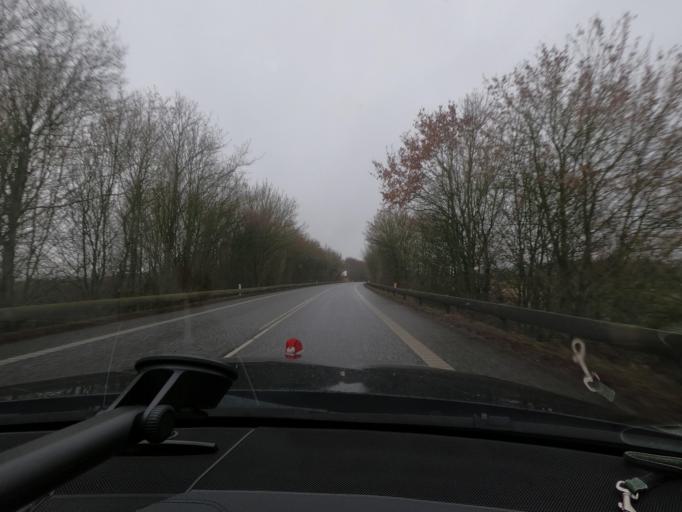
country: DK
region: South Denmark
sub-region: Sonderborg Kommune
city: Horuphav
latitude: 54.9103
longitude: 9.9176
